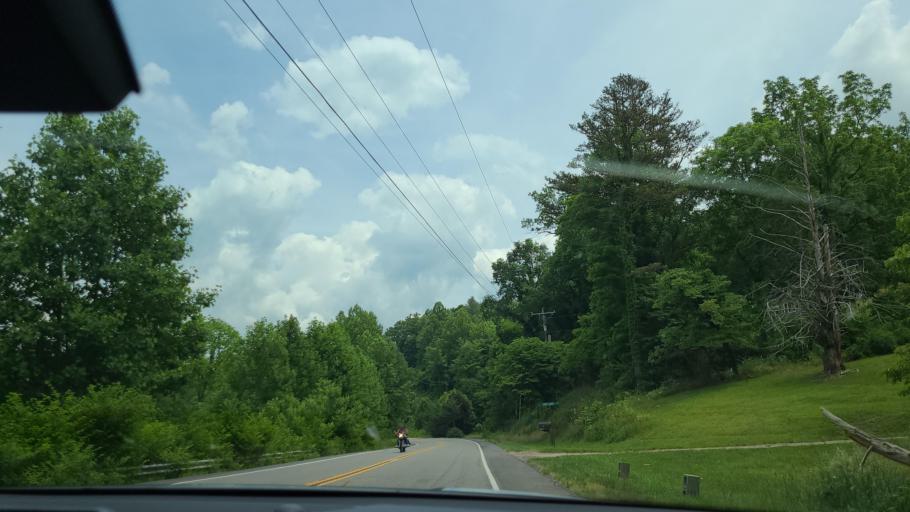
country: US
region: North Carolina
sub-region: Macon County
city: Franklin
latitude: 35.1554
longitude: -83.3147
